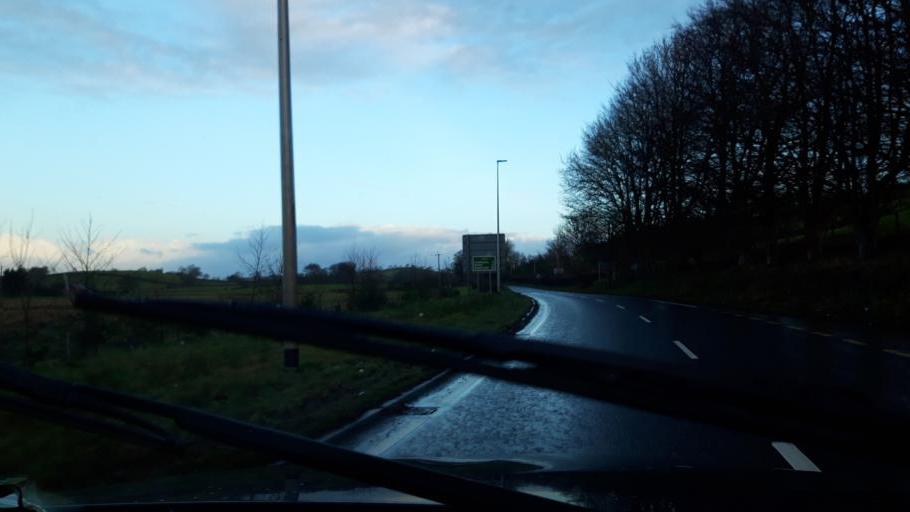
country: GB
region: Northern Ireland
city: Dunloy
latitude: 55.0175
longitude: -6.3671
